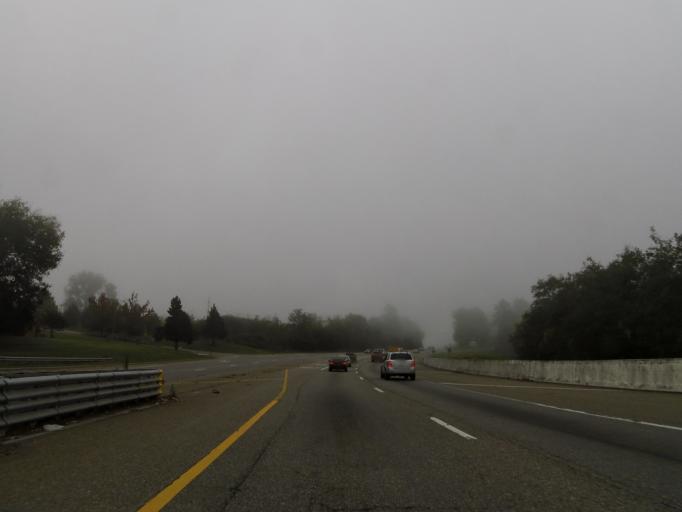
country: US
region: Tennessee
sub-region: Blount County
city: Eagleton Village
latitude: 35.8721
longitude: -83.9613
